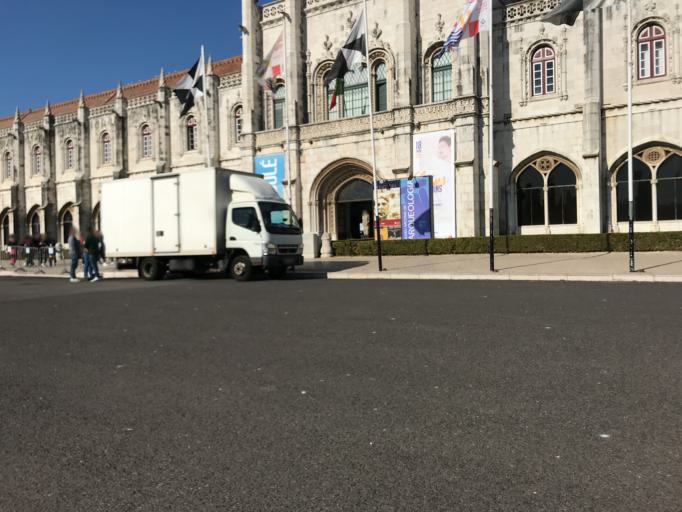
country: PT
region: Lisbon
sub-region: Oeiras
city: Alges
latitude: 38.6971
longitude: -9.2067
